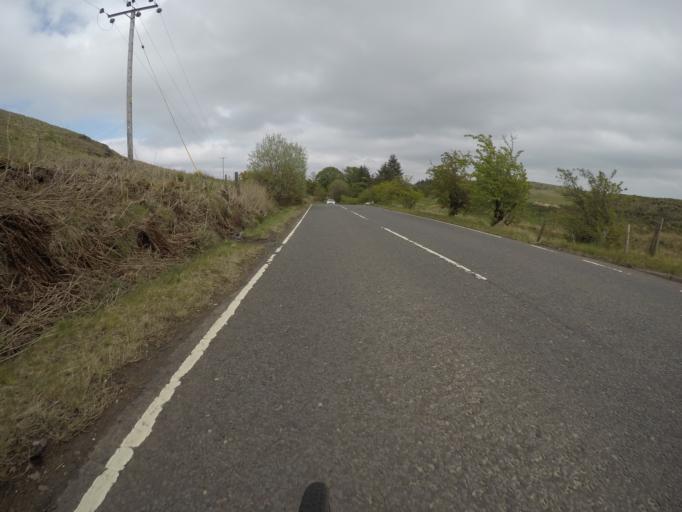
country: GB
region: Scotland
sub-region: East Renfrewshire
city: Neilston
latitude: 55.7477
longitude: -4.3959
